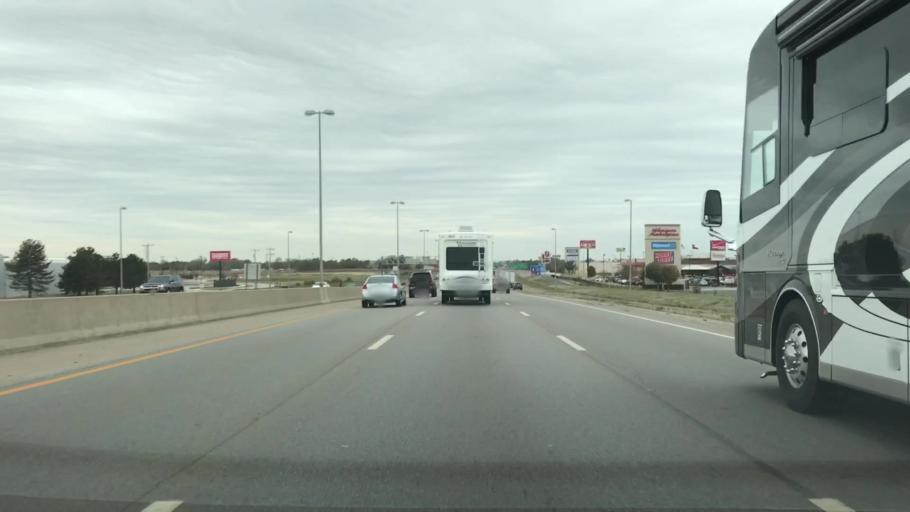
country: US
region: Oklahoma
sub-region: Oklahoma County
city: Bethany
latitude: 35.4602
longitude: -97.6201
